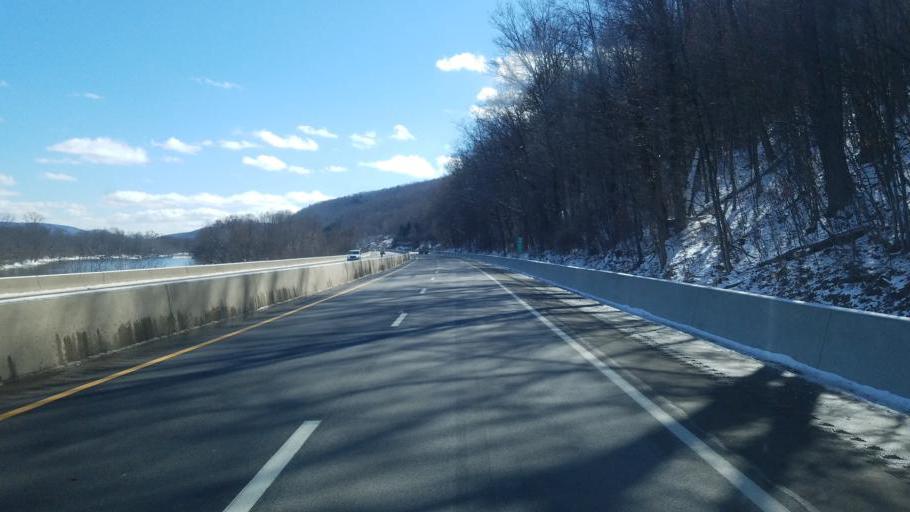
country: US
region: New York
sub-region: Cattaraugus County
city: Salamanca
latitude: 42.1318
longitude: -78.6664
